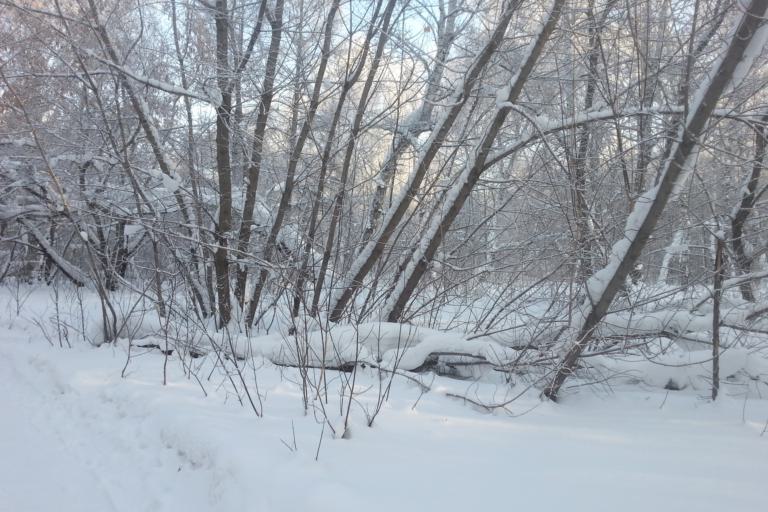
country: RU
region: Altai Krai
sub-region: Gorod Barnaulskiy
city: Barnaul
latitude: 53.3687
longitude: 83.7207
